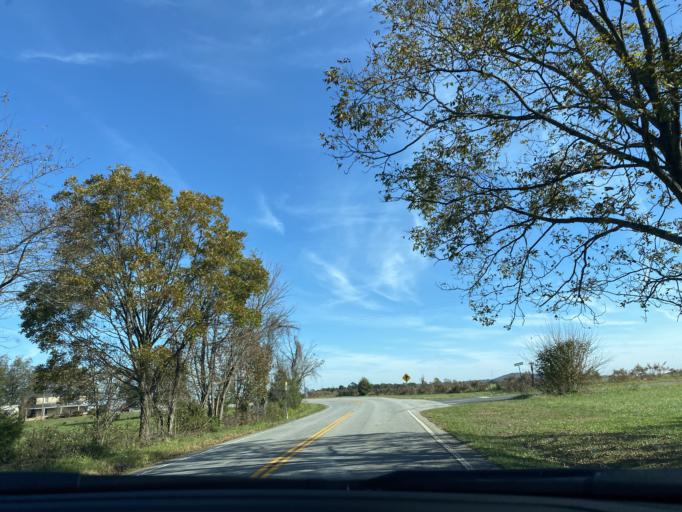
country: US
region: South Carolina
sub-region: Spartanburg County
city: Mayo
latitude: 35.0866
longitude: -81.8108
